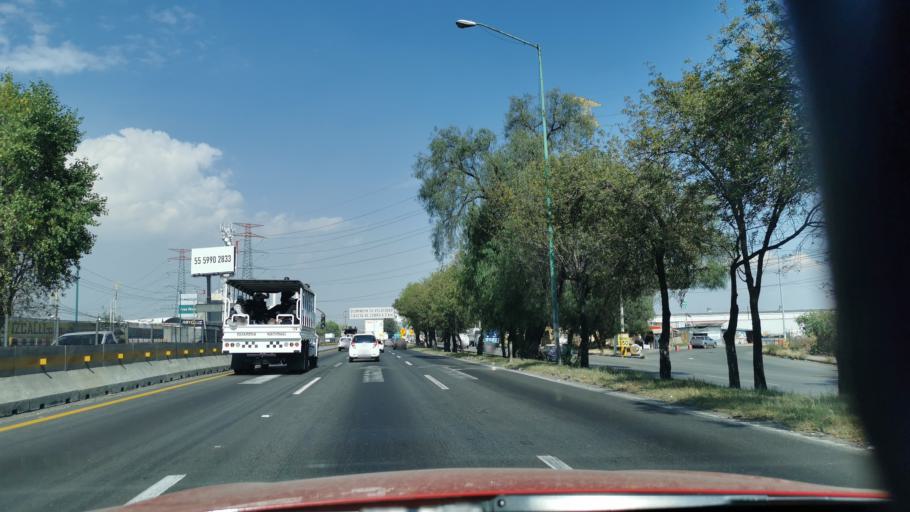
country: MX
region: Mexico
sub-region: Cuautitlan
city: San Jose del Puente
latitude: 19.6929
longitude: -99.2037
